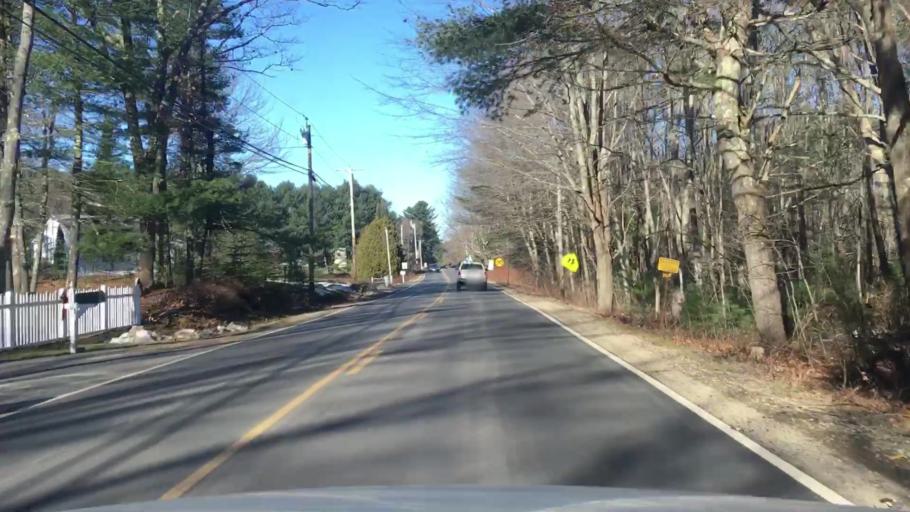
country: US
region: Maine
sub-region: York County
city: Arundel
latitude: 43.4140
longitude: -70.4992
